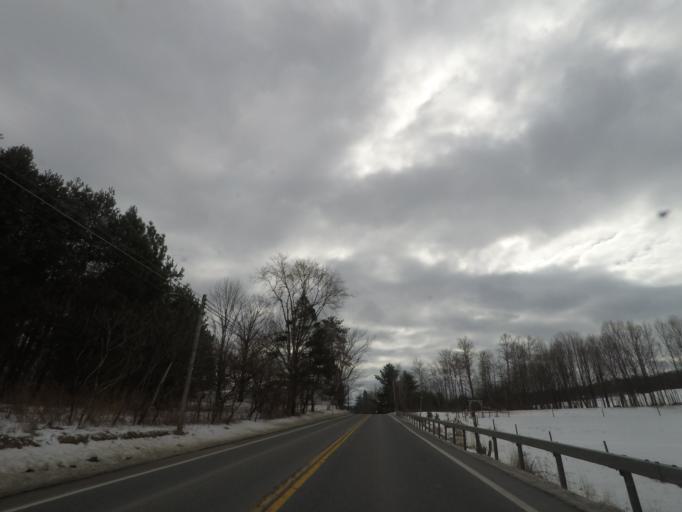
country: US
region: New York
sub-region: Washington County
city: Greenwich
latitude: 43.0723
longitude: -73.4814
